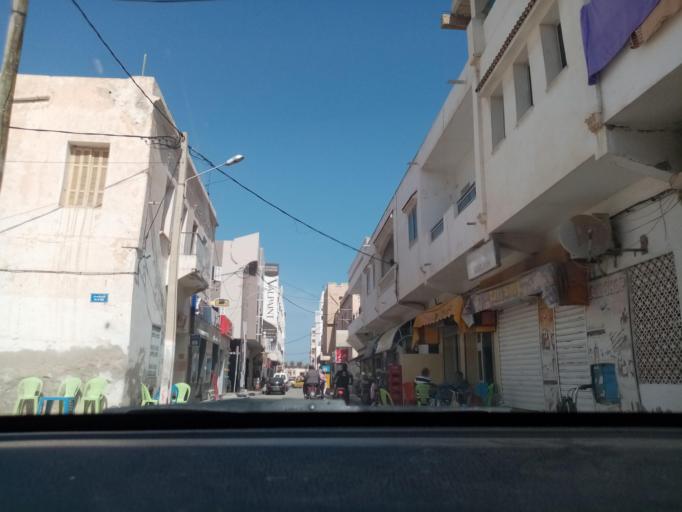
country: TN
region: Qabis
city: Gabes
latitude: 33.8866
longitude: 10.1046
